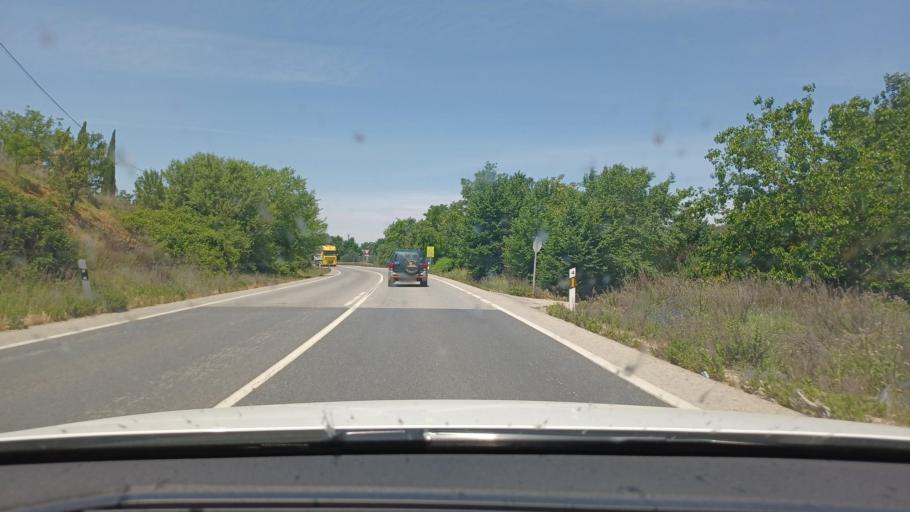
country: ES
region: Madrid
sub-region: Provincia de Madrid
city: Meco
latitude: 40.5382
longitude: -3.3035
